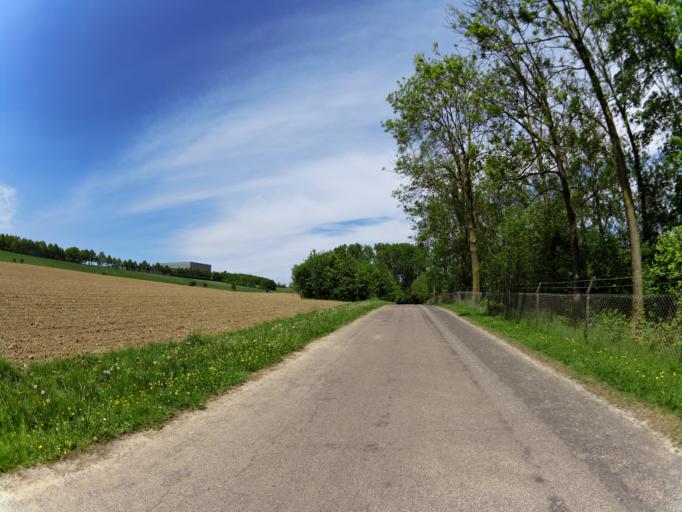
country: NL
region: Limburg
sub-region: Gemeente Kerkrade
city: Kerkrade
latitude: 50.8824
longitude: 6.0473
